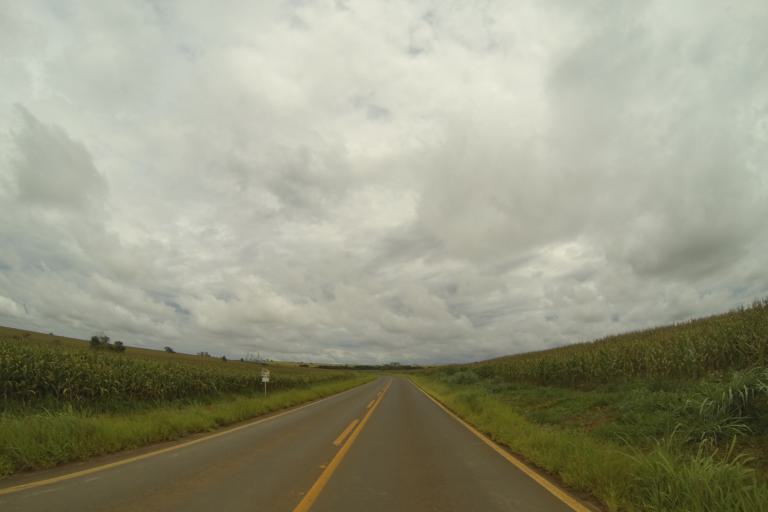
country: BR
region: Minas Gerais
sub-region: Bambui
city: Bambui
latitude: -20.0977
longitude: -46.0941
